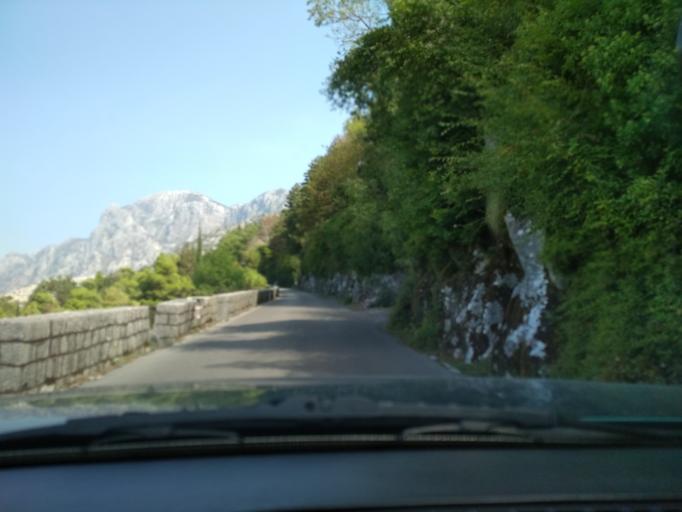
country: ME
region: Kotor
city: Kotor
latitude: 42.4043
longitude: 18.7759
